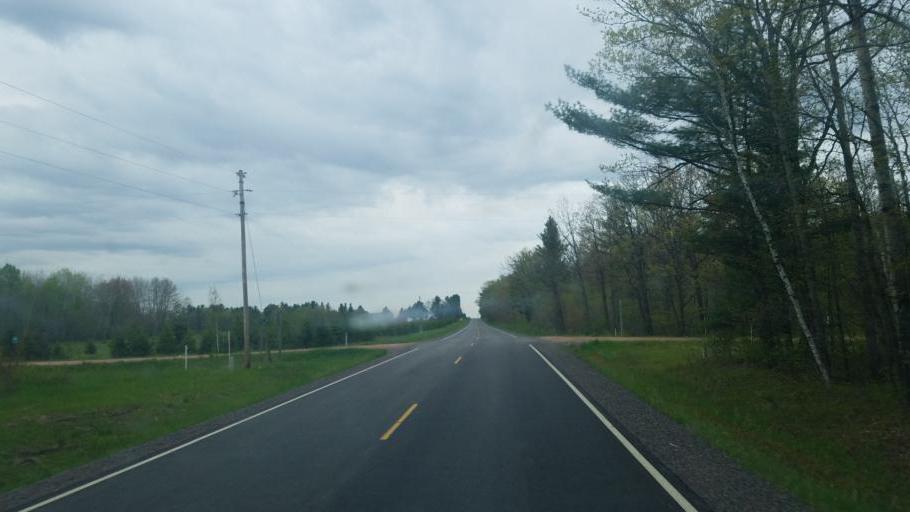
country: US
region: Wisconsin
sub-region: Wood County
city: Marshfield
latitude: 44.4964
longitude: -90.2793
